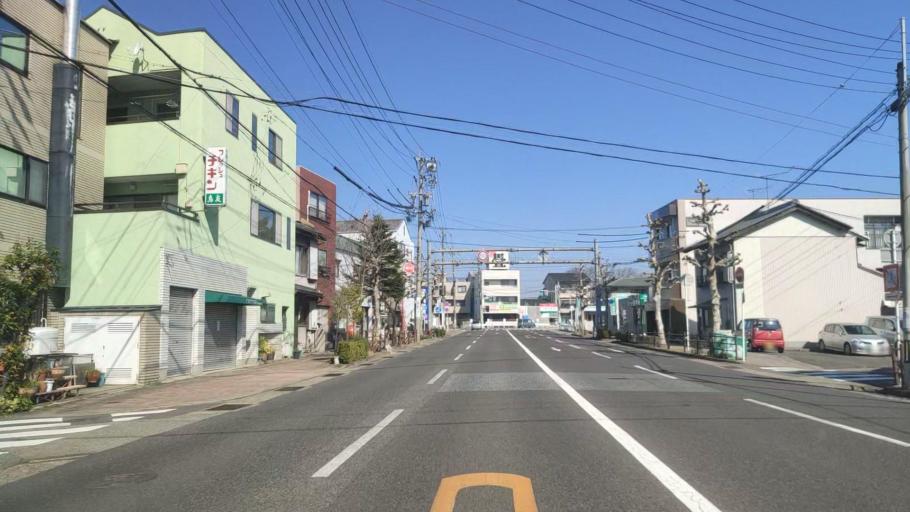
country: JP
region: Gifu
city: Gifu-shi
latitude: 35.4285
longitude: 136.7591
